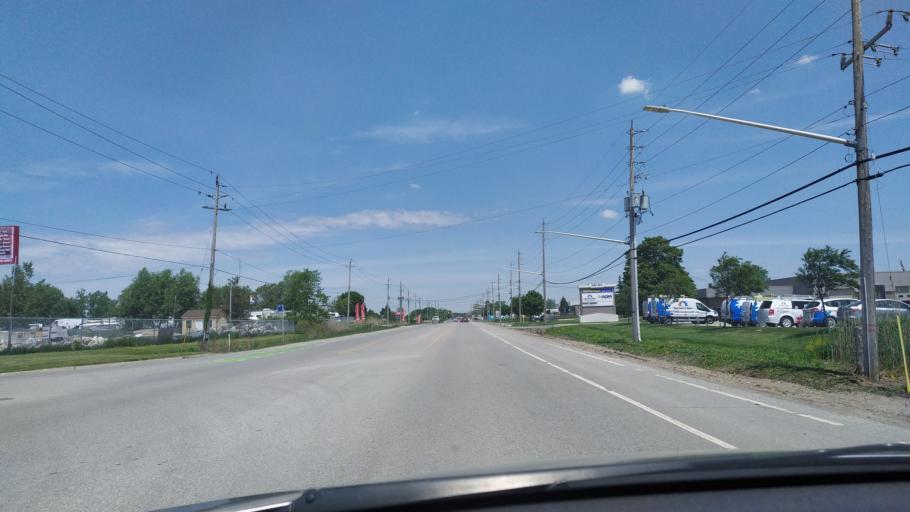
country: CA
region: Ontario
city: London
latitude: 42.9275
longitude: -81.2488
